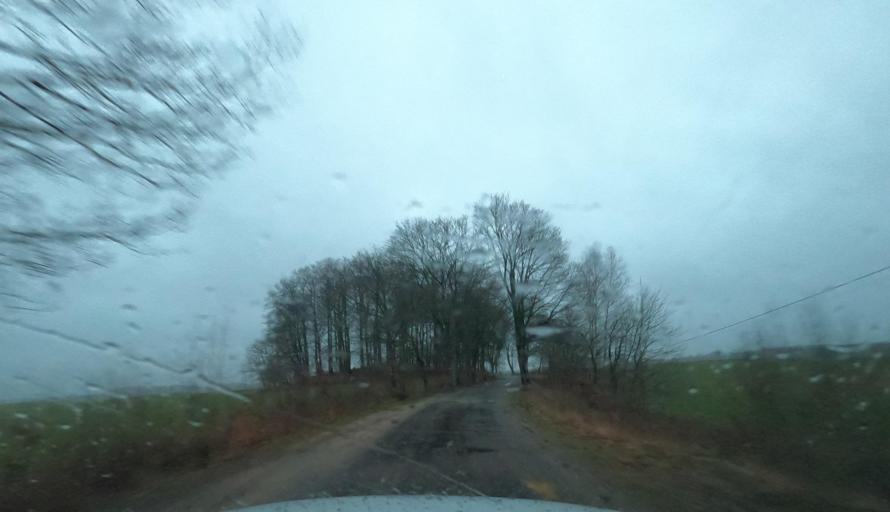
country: PL
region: West Pomeranian Voivodeship
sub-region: Powiat szczecinecki
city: Borne Sulinowo
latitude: 53.6870
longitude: 16.4815
